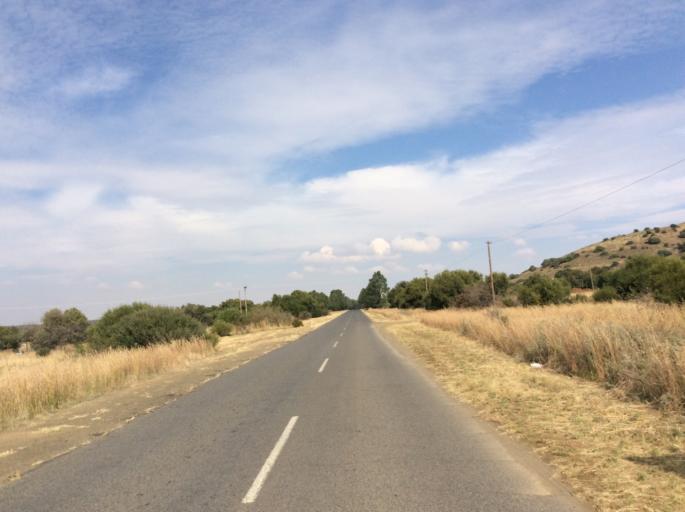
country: ZA
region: Orange Free State
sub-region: Xhariep District Municipality
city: Dewetsdorp
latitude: -29.5642
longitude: 26.6660
